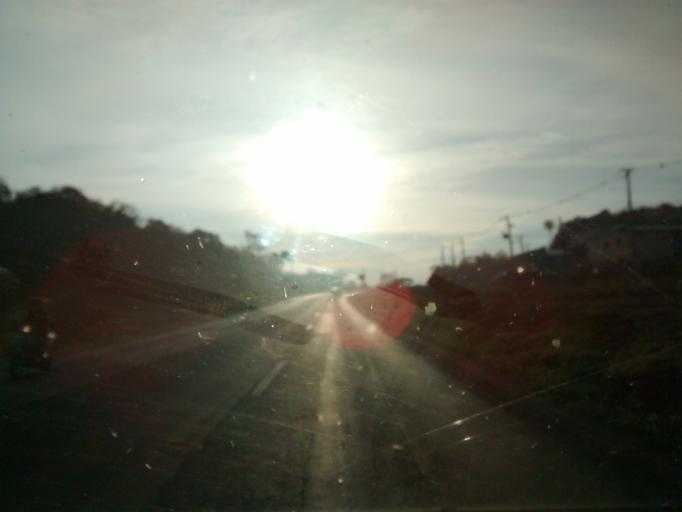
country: BR
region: Parana
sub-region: Francisco Beltrao
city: Francisco Beltrao
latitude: -26.1465
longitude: -52.9987
